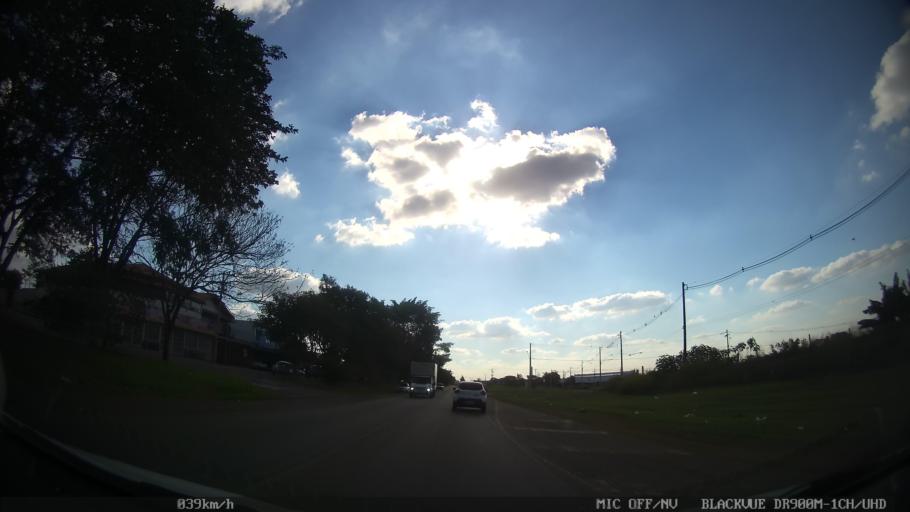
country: BR
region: Sao Paulo
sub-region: Santa Barbara D'Oeste
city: Santa Barbara d'Oeste
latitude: -22.7709
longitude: -47.3836
